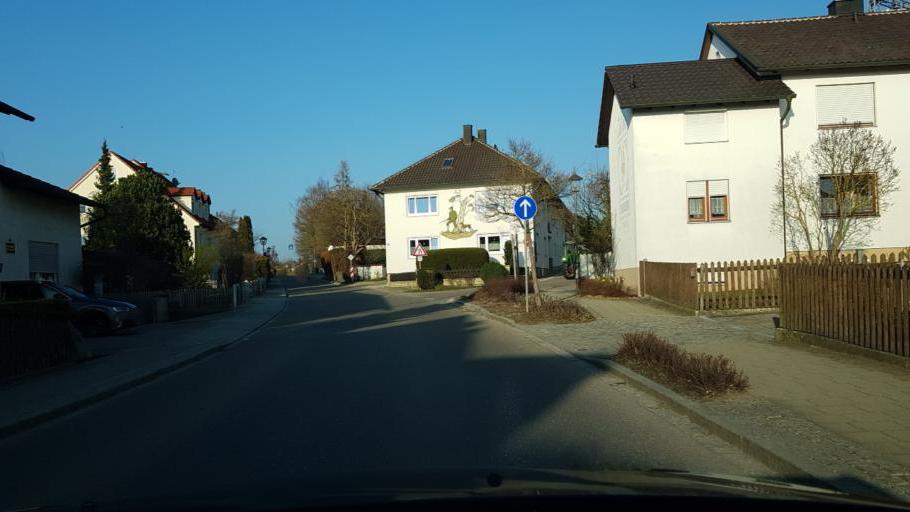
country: DE
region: Bavaria
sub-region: Upper Bavaria
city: Altomunster
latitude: 48.3905
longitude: 11.2584
